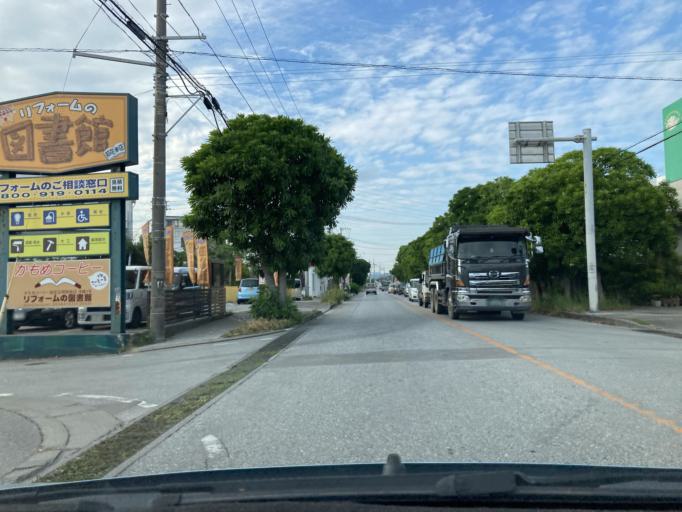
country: JP
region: Okinawa
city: Okinawa
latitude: 26.3676
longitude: 127.8164
